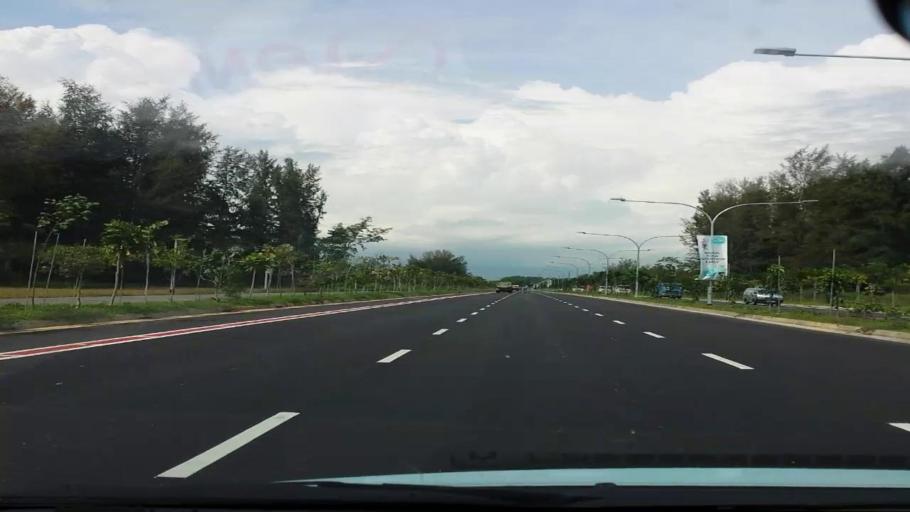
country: SG
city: Singapore
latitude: 1.3263
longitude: 104.0191
